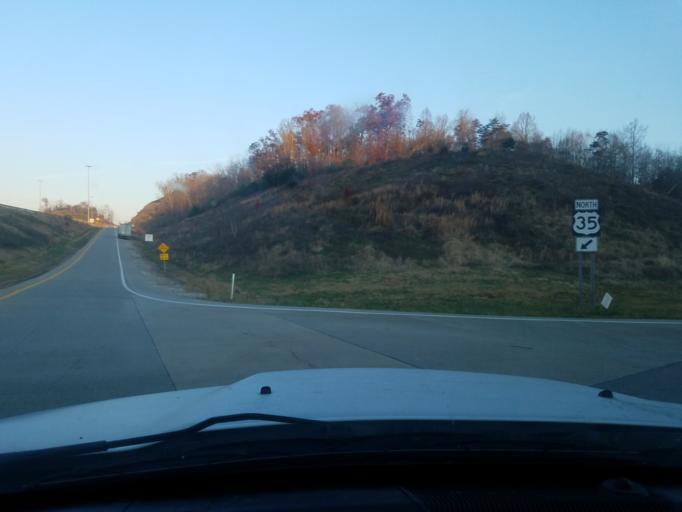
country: US
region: West Virginia
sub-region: Putnam County
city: Teays Valley
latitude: 38.4825
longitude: -81.9275
